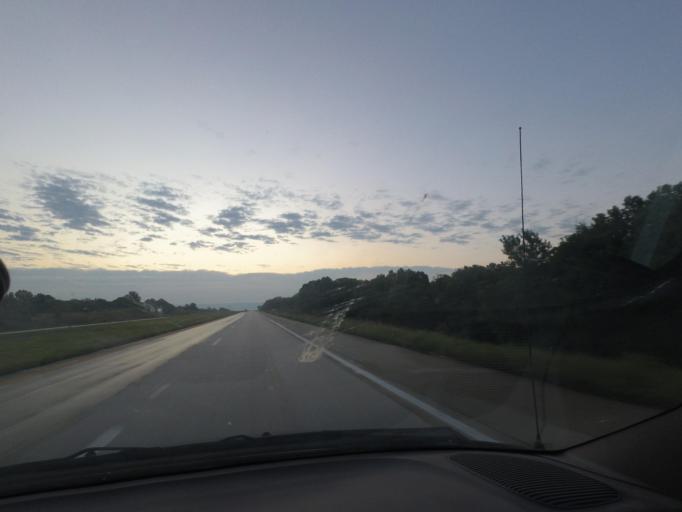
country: US
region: Missouri
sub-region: Macon County
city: Macon
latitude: 39.7588
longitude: -92.6548
